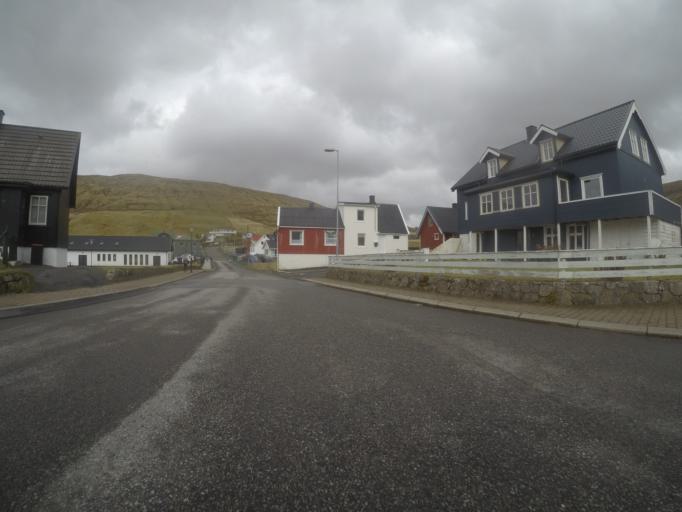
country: FO
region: Vagar
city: Midvagur
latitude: 62.0553
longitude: -7.1489
